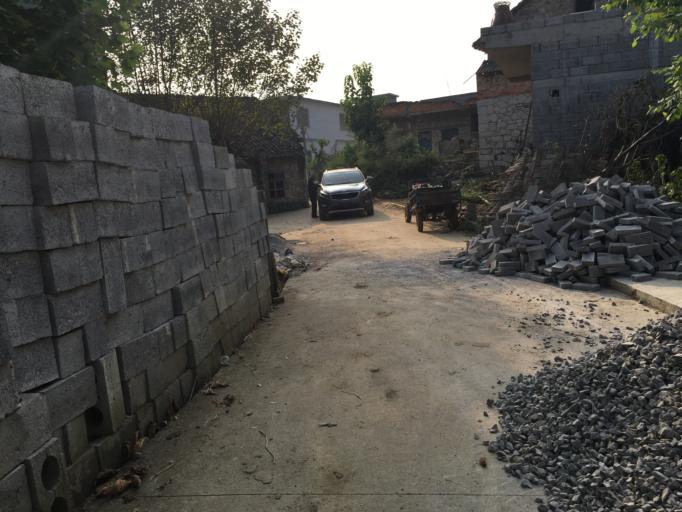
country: CN
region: Guangxi Zhuangzu Zizhiqu
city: Xinzhou
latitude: 25.4389
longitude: 105.6331
